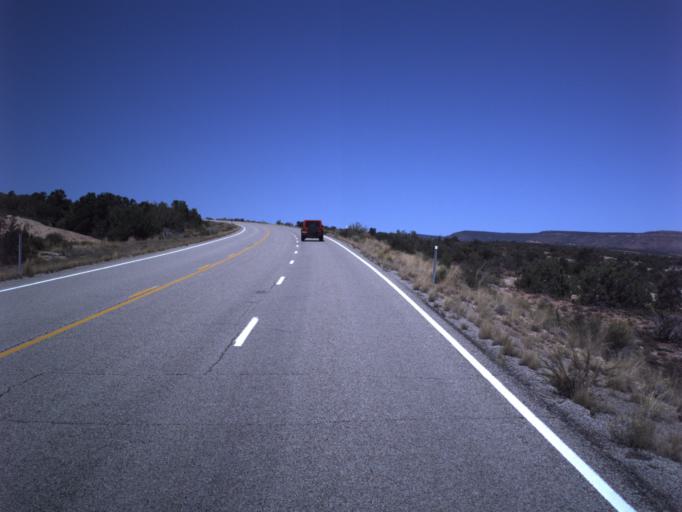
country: US
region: Utah
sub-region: San Juan County
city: Blanding
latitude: 37.5210
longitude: -109.6698
